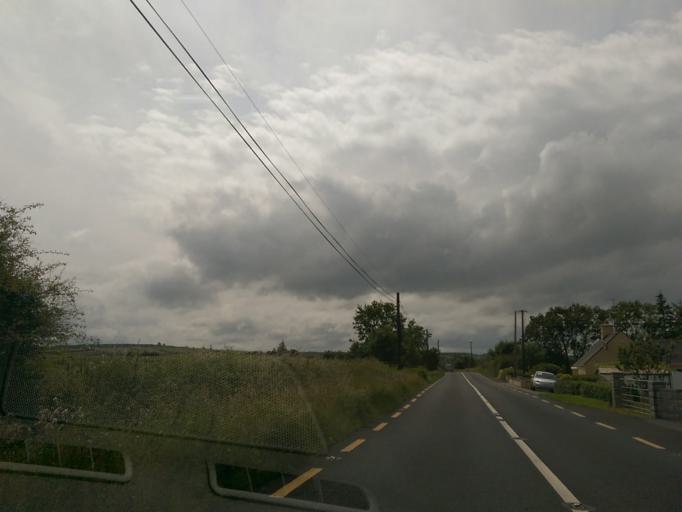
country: IE
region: Munster
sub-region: An Clar
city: Kilrush
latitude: 52.6908
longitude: -9.3510
